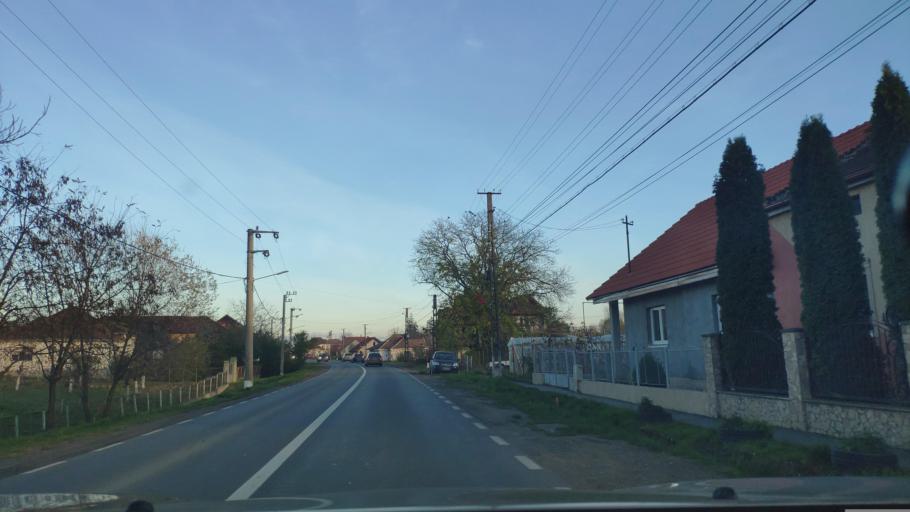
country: RO
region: Satu Mare
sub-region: Comuna Odoreu
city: Odoreu
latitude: 47.7963
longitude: 22.9809
